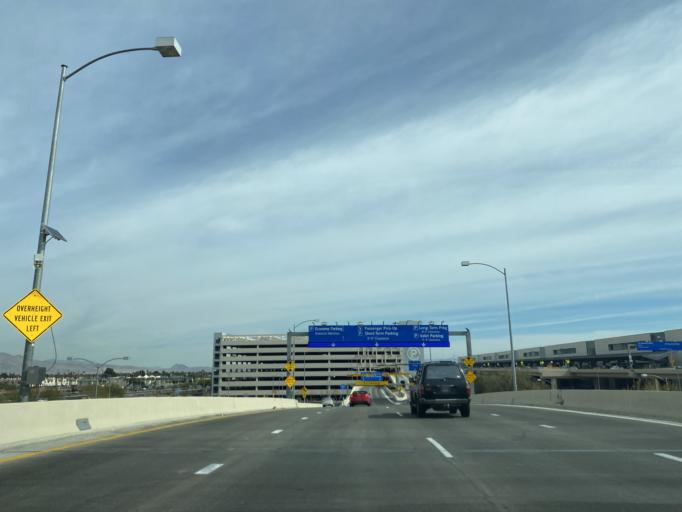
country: US
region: Nevada
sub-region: Clark County
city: Paradise
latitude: 36.0874
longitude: -115.1417
